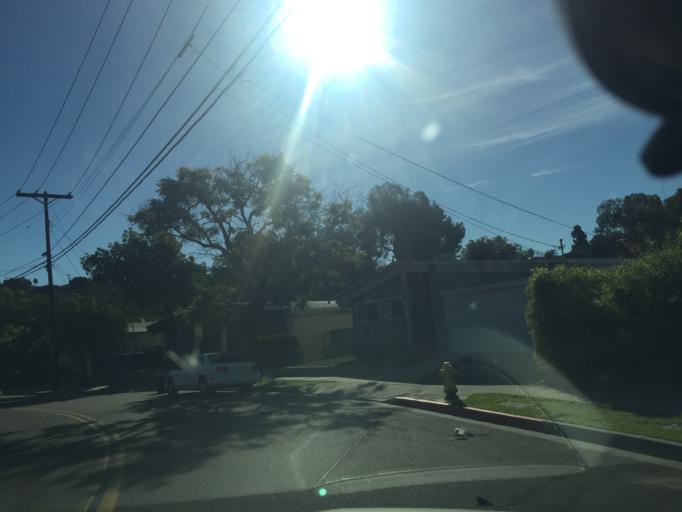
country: US
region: California
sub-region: San Diego County
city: Lemon Grove
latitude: 32.7681
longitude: -117.0805
